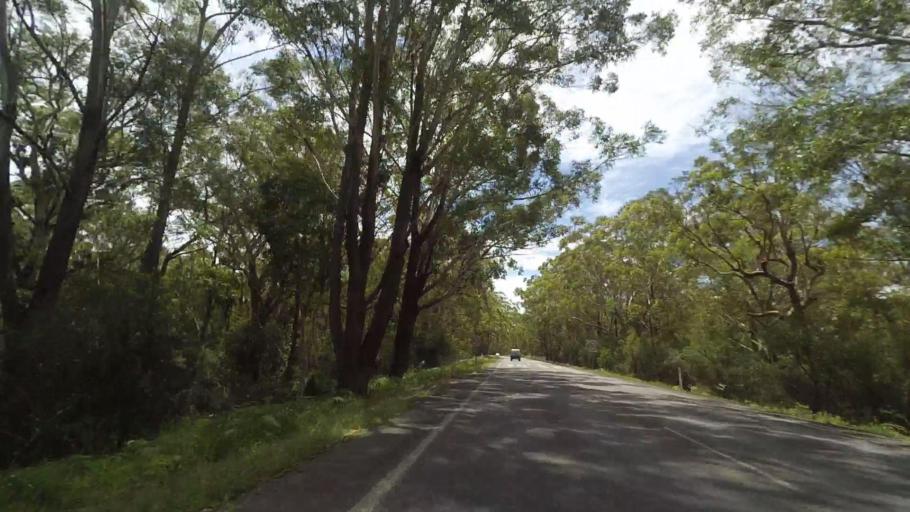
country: AU
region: New South Wales
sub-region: Port Stephens Shire
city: Medowie
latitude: -32.7735
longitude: 151.8684
